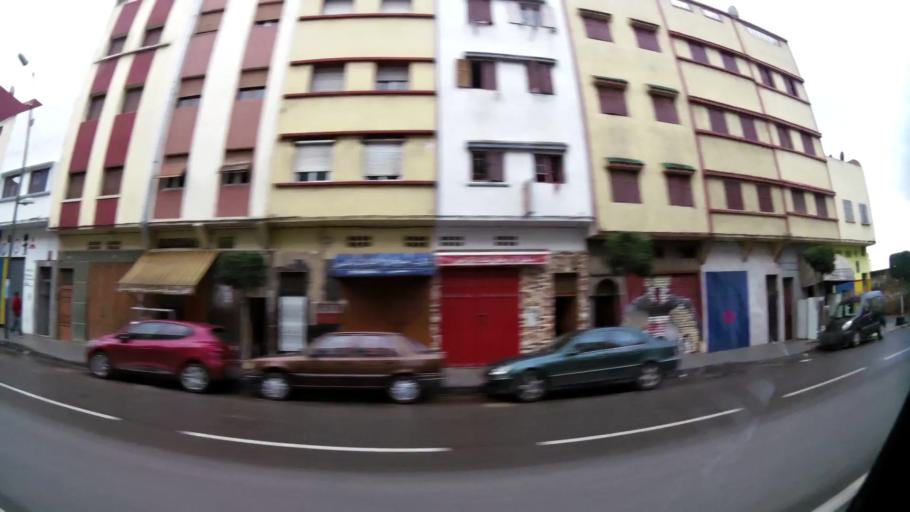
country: MA
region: Grand Casablanca
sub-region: Casablanca
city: Casablanca
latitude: 33.5523
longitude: -7.5857
